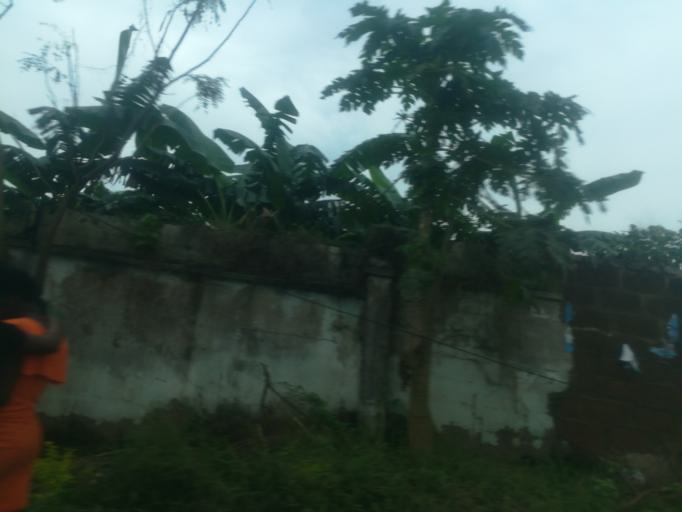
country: NG
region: Oyo
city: Ibadan
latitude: 7.3977
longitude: 3.9244
